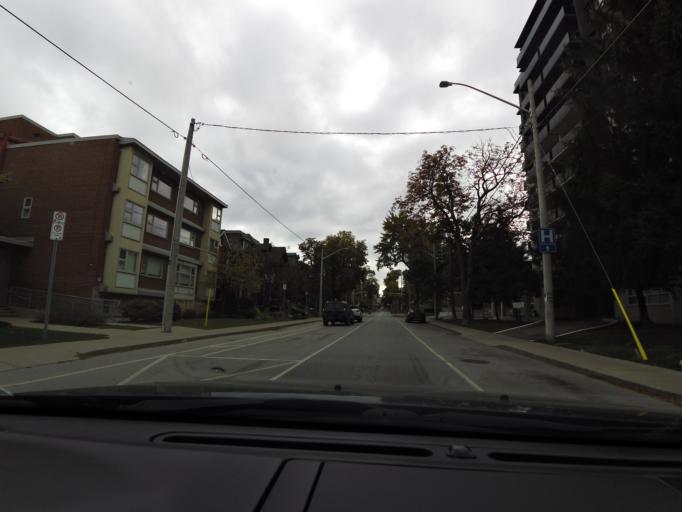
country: CA
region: Ontario
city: Hamilton
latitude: 43.2507
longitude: -79.8803
